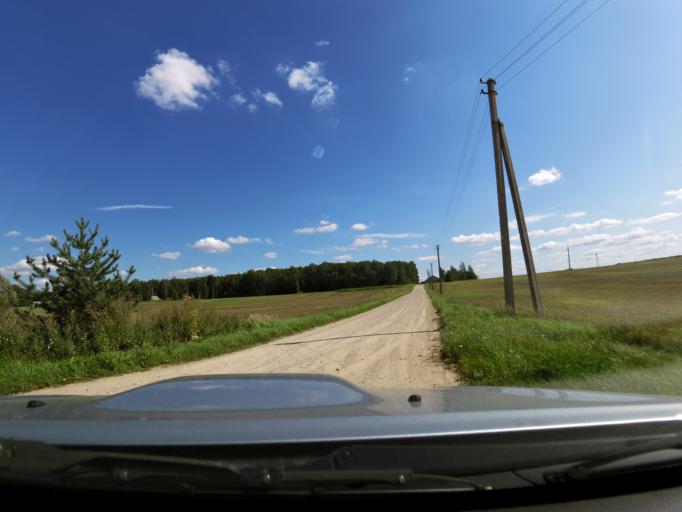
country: LT
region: Panevezys
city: Pasvalys
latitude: 56.0352
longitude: 24.3623
